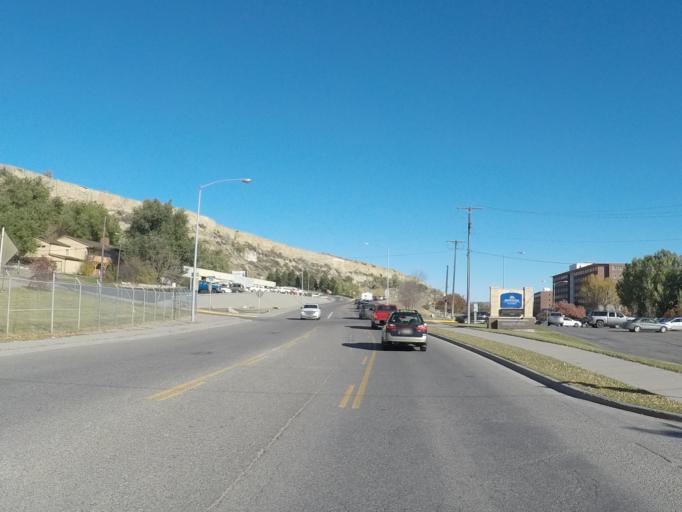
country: US
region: Montana
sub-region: Yellowstone County
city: Billings
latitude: 45.7983
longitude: -108.5252
